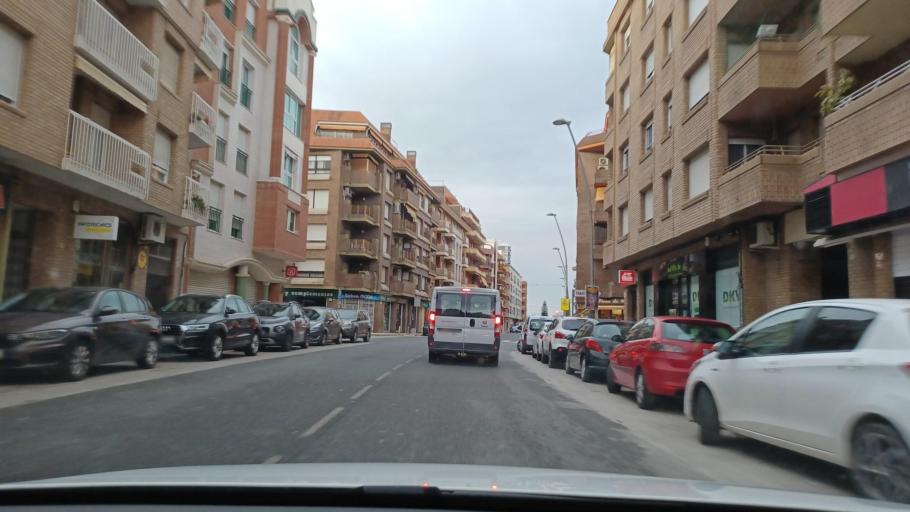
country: ES
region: Catalonia
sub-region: Provincia de Tarragona
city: Tortosa
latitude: 40.8051
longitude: 0.5206
